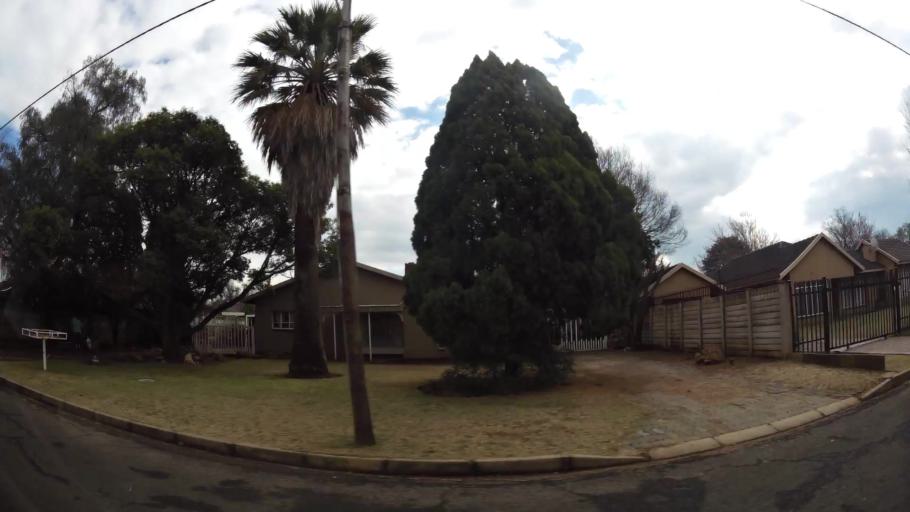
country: ZA
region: Gauteng
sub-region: Sedibeng District Municipality
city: Vereeniging
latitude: -26.6429
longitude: 27.9787
